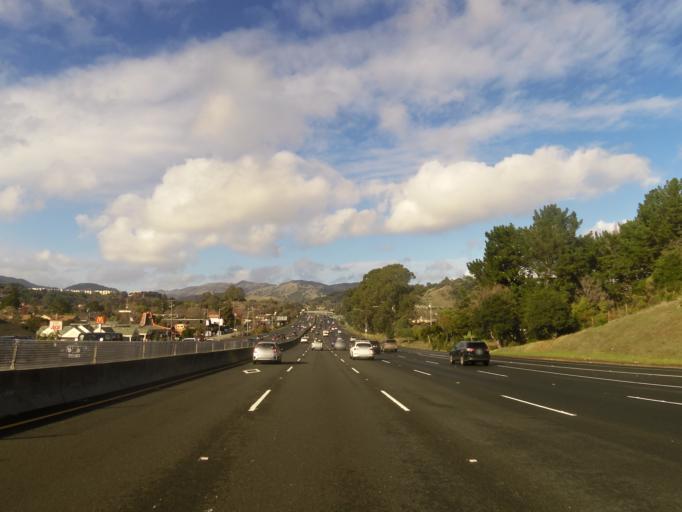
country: US
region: California
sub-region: Marin County
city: Santa Venetia
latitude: 37.9956
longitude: -122.5332
